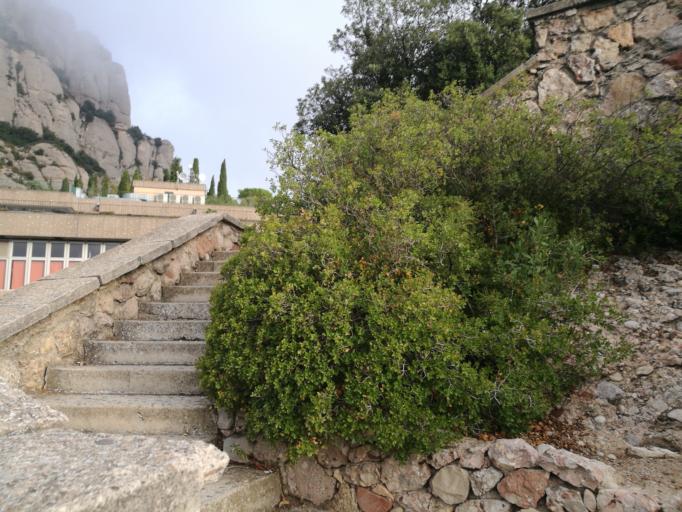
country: ES
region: Catalonia
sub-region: Provincia de Barcelona
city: Monistrol de Montserrat
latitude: 41.5939
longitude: 1.8412
